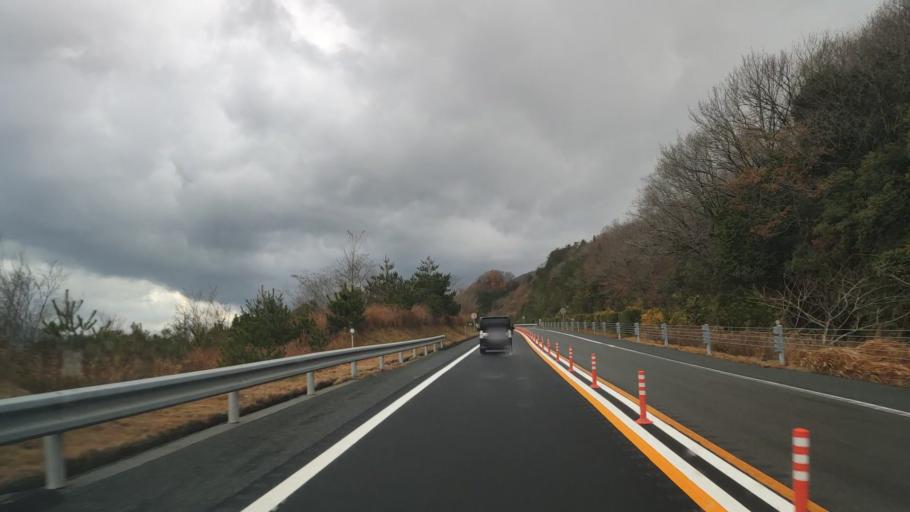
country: JP
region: Tokushima
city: Wakimachi
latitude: 34.0542
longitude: 134.0114
